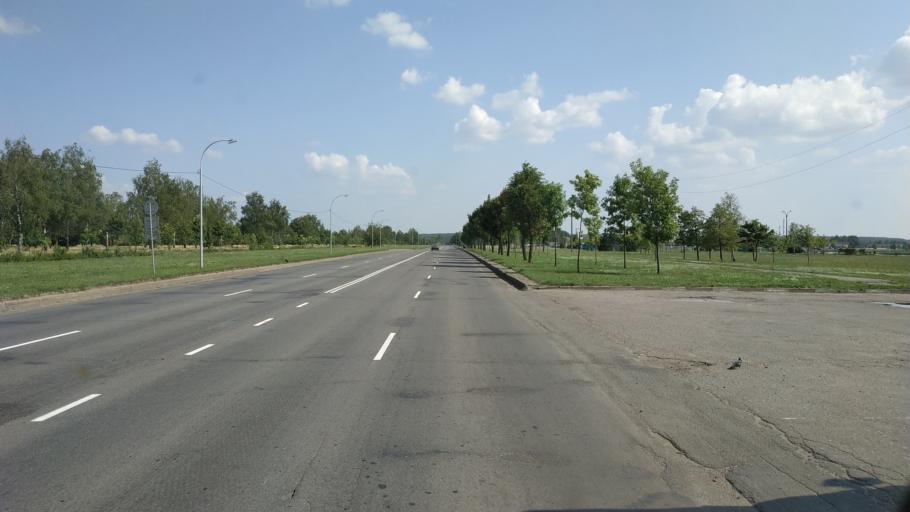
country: BY
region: Mogilev
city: Buynichy
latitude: 53.8636
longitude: 30.3197
